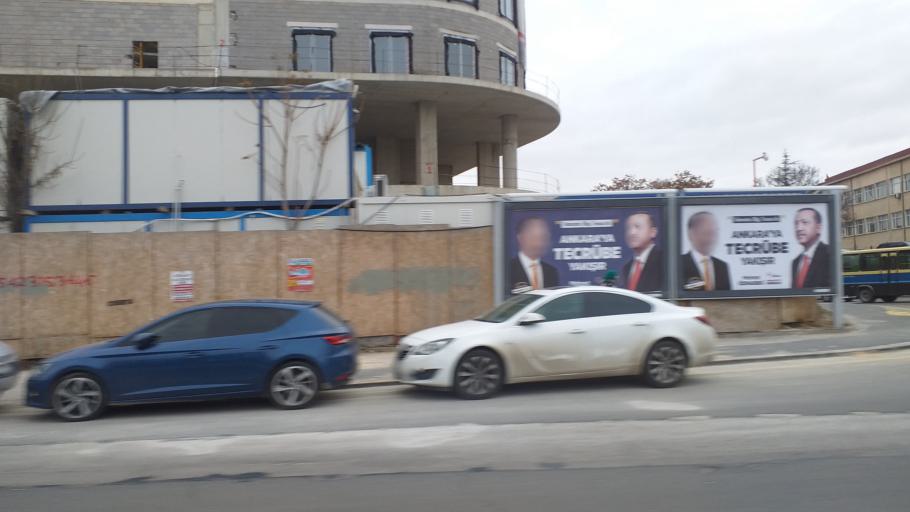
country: TR
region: Ankara
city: Ankara
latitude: 39.9422
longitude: 32.8253
